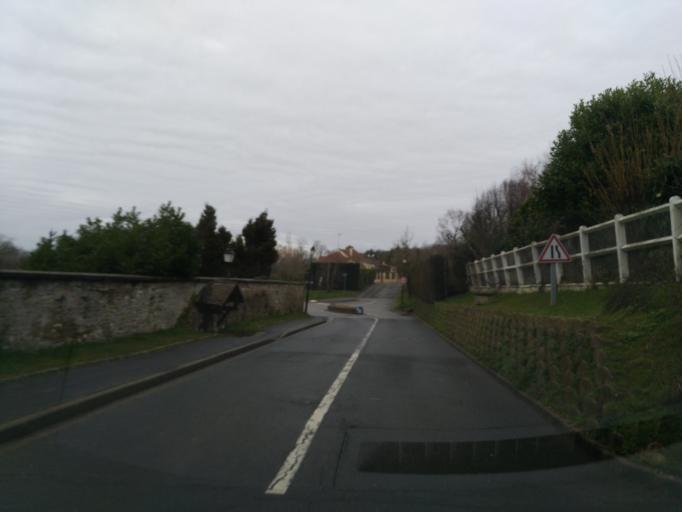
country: FR
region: Ile-de-France
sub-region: Departement des Yvelines
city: Saint-Nom-la-Breteche
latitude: 48.8698
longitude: 2.0152
